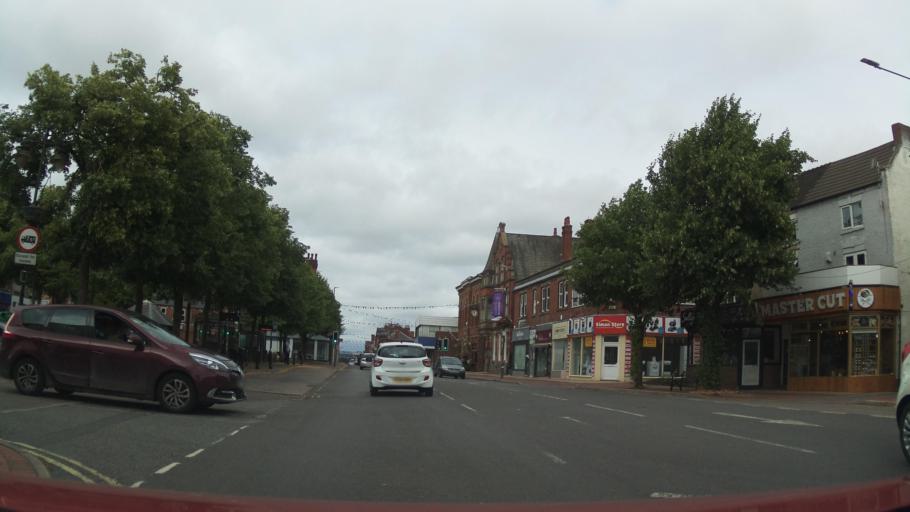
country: GB
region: England
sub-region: Derbyshire
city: Heanor
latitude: 53.0136
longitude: -1.3528
